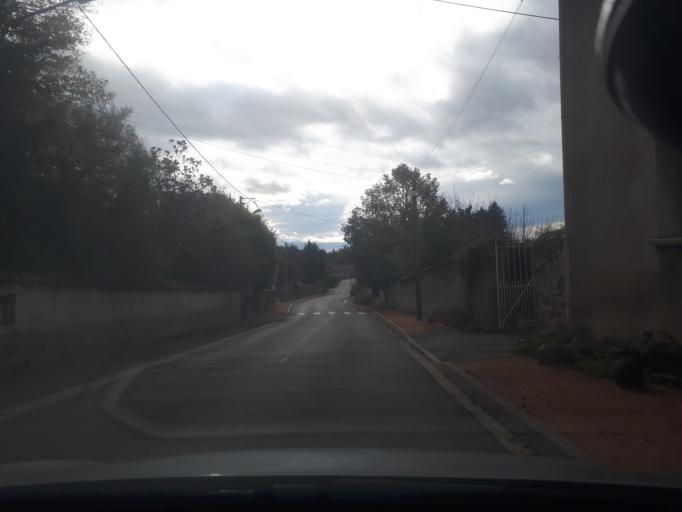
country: FR
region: Rhone-Alpes
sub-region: Departement de la Loire
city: Bellegarde-en-Forez
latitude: 45.6753
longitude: 4.2944
